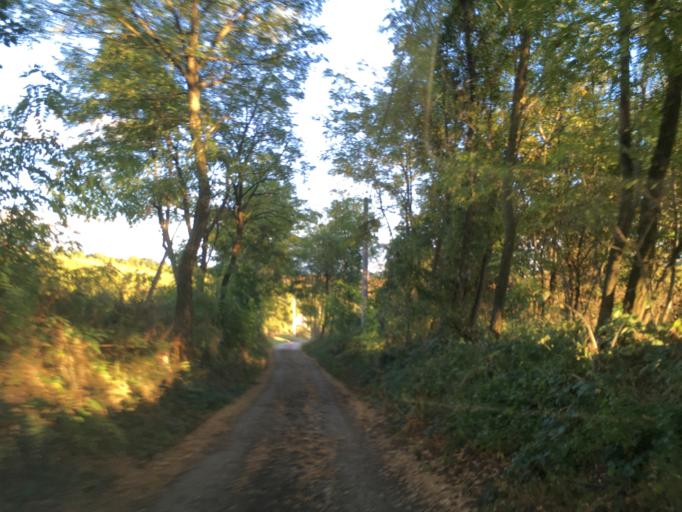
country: SK
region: Nitriansky
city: Svodin
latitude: 47.9159
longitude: 18.4351
